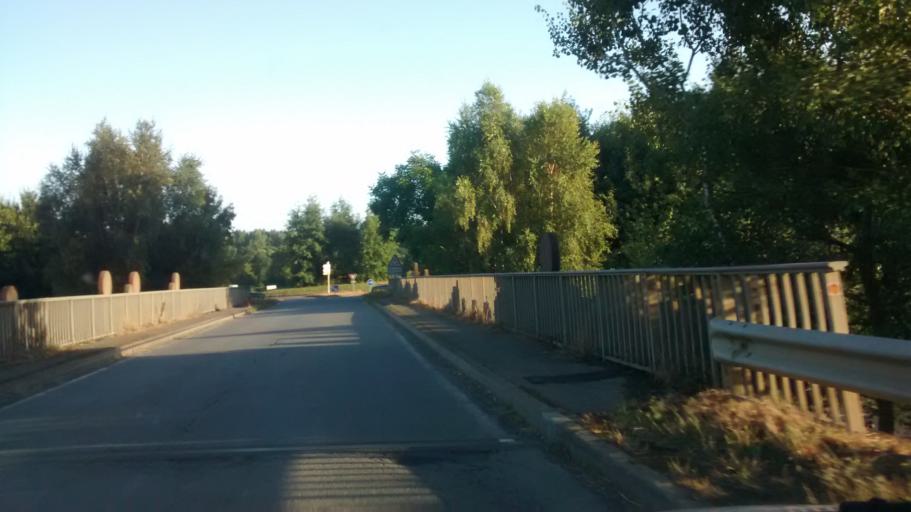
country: FR
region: Brittany
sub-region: Departement d'Ille-et-Vilaine
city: Plerguer
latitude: 48.5441
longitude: -1.8606
